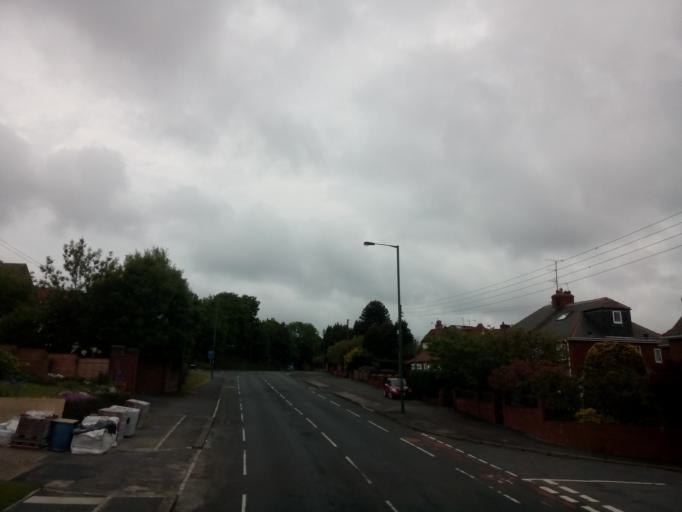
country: GB
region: England
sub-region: County Durham
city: Chester-le-Street
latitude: 54.8636
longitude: -1.5739
